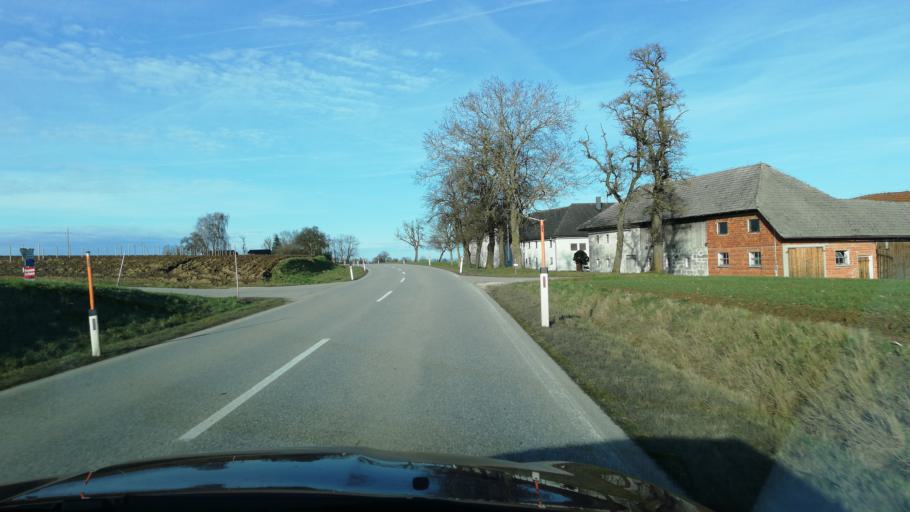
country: AT
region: Upper Austria
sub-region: Politischer Bezirk Kirchdorf an der Krems
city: Kremsmunster
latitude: 47.9841
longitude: 14.0795
